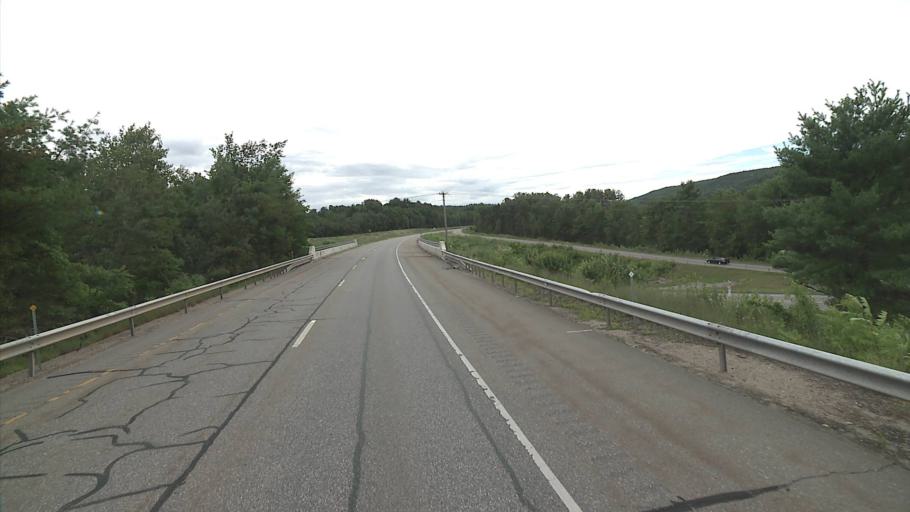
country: US
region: Connecticut
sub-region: Litchfield County
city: Winsted
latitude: 41.8789
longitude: -73.0719
